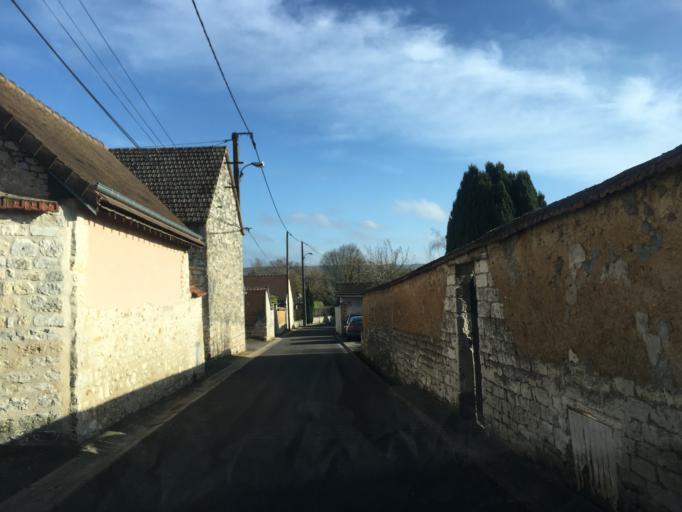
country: FR
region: Haute-Normandie
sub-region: Departement de l'Eure
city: Saint-Just
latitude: 49.1091
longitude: 1.4379
